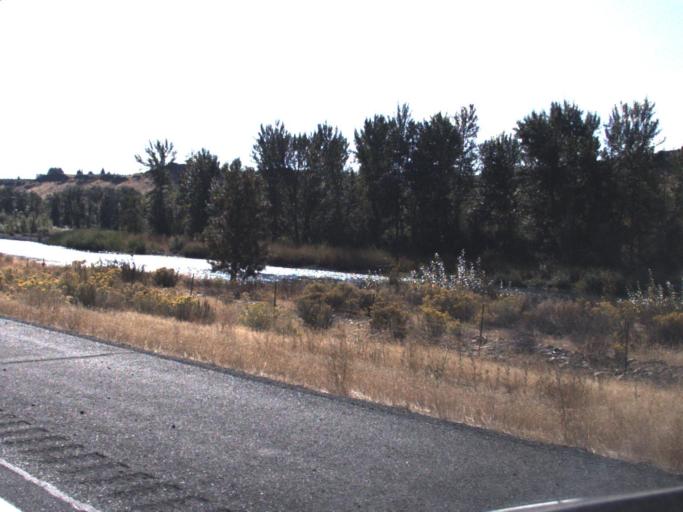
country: US
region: Washington
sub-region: Yakima County
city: Gleed
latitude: 46.6825
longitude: -120.6509
